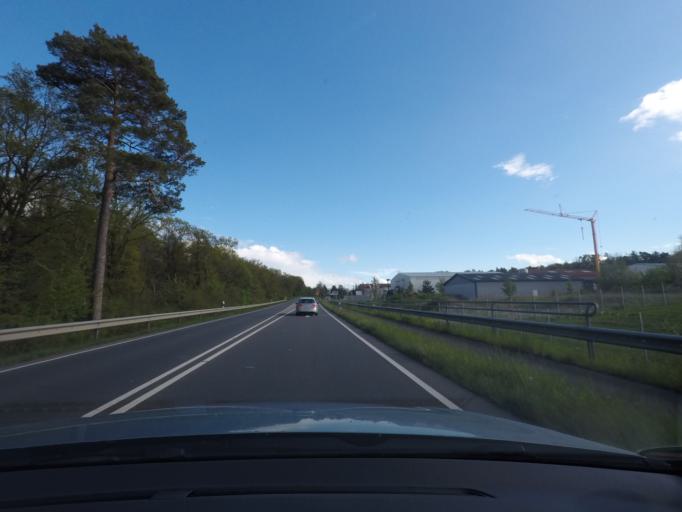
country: DE
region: Lower Saxony
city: Mariental
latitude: 52.2531
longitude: 10.9926
